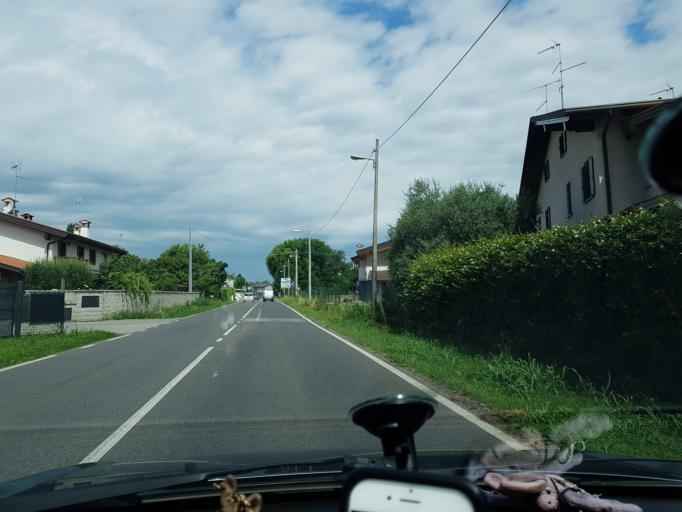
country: IT
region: Friuli Venezia Giulia
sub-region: Provincia di Gorizia
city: Pieris
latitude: 45.8056
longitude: 13.4434
